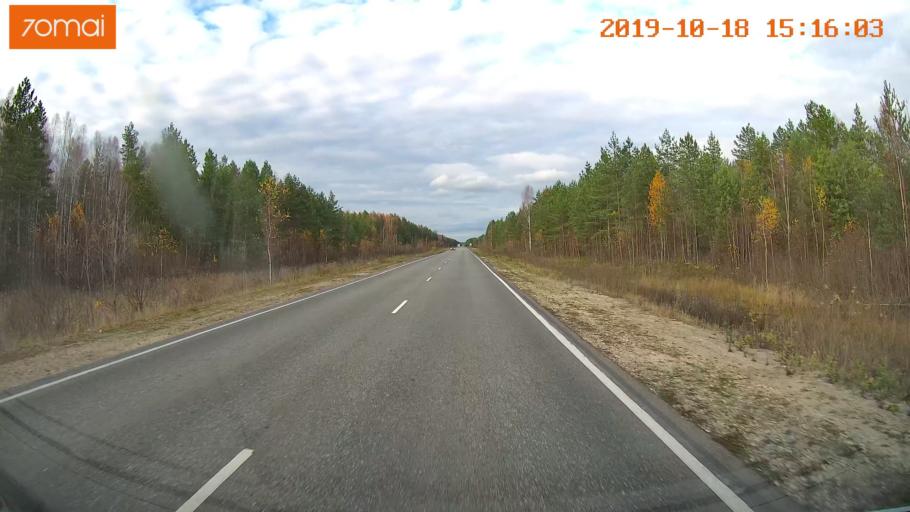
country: RU
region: Vladimir
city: Gus'-Khrustal'nyy
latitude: 55.6294
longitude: 40.7239
